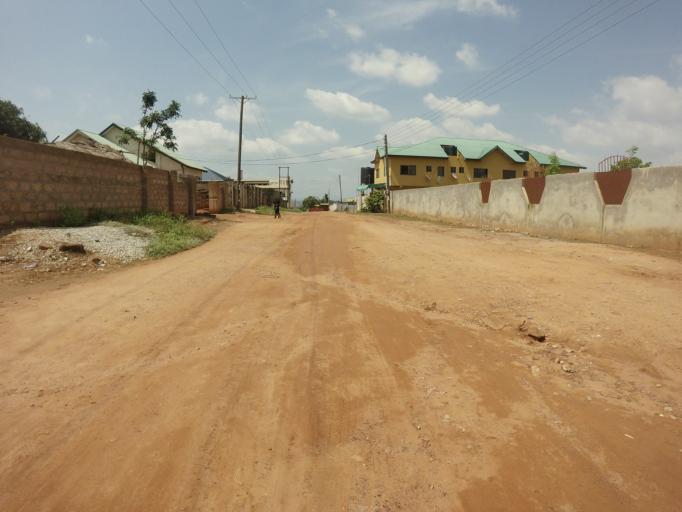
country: GH
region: Greater Accra
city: Gbawe
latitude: 5.6166
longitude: -0.3128
